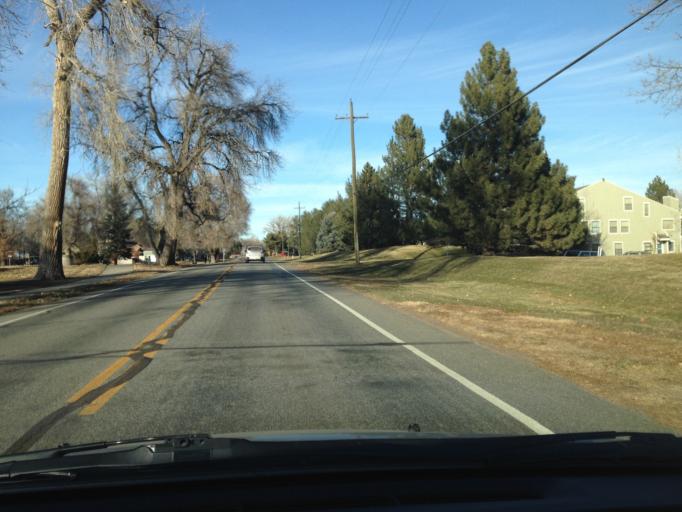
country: US
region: Colorado
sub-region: Boulder County
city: Niwot
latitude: 40.0975
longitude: -105.1690
